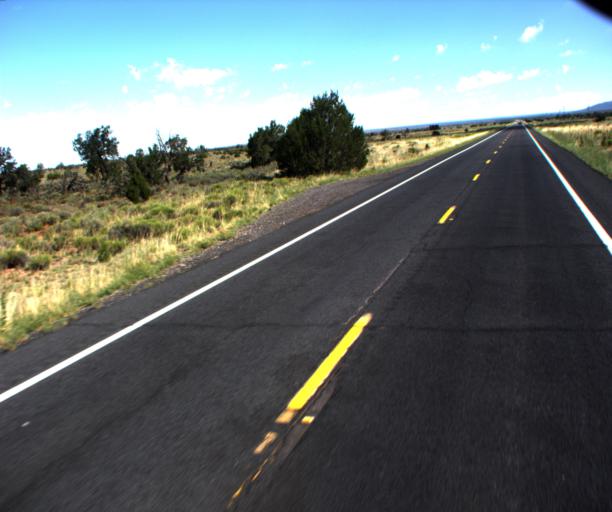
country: US
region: Arizona
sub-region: Coconino County
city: Grand Canyon Village
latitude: 35.6751
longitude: -112.1363
